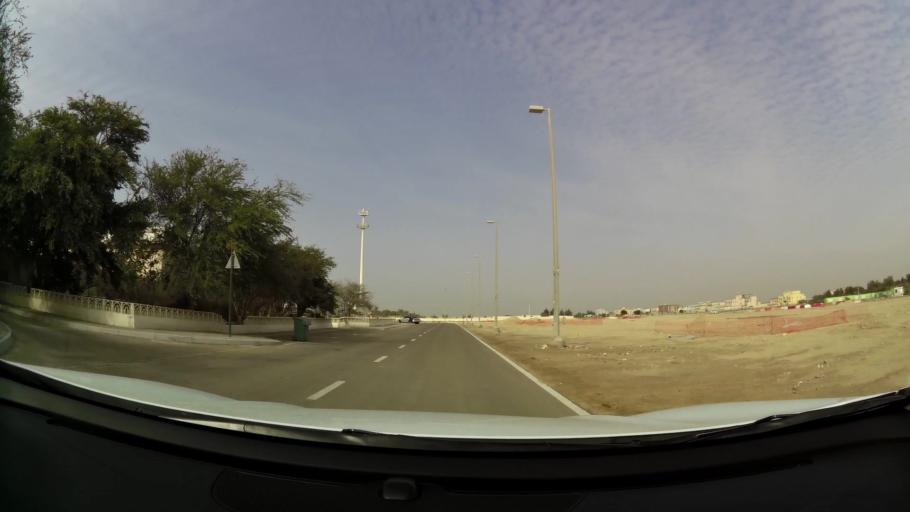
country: AE
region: Abu Dhabi
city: Abu Dhabi
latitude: 24.6157
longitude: 54.7059
